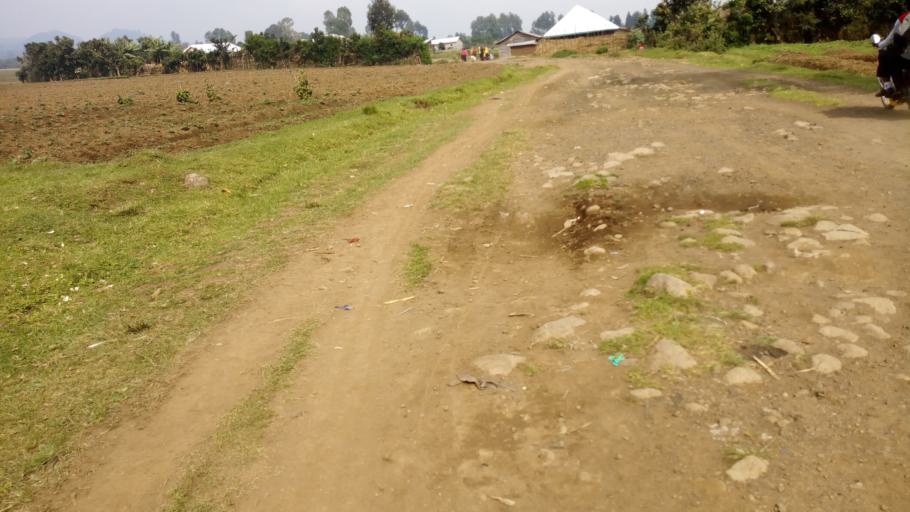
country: UG
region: Western Region
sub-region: Kisoro District
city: Kisoro
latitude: -1.3321
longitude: 29.6101
